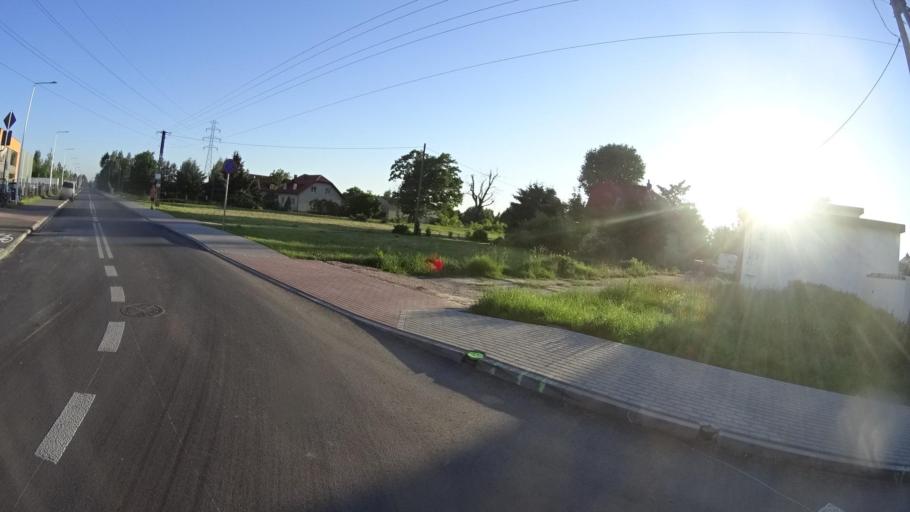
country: PL
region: Masovian Voivodeship
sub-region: Powiat warszawski zachodni
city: Stare Babice
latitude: 52.2658
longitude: 20.8445
